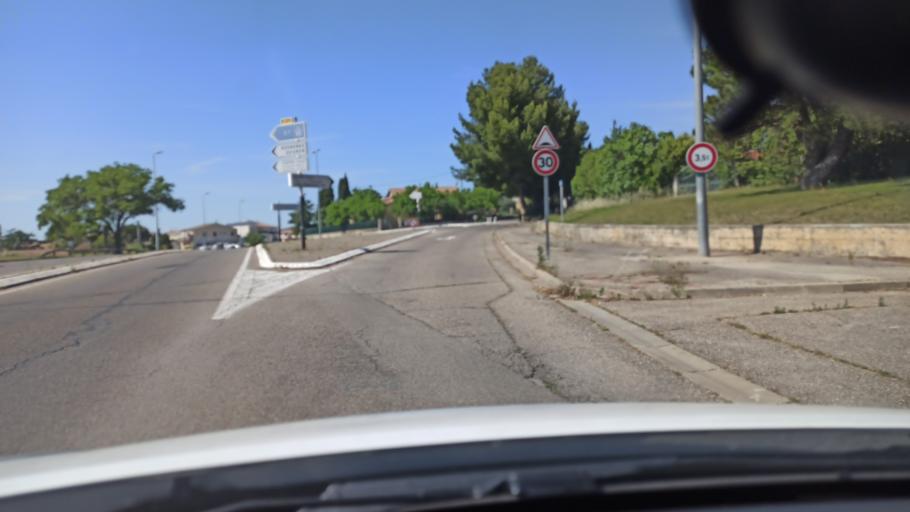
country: FR
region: Provence-Alpes-Cote d'Azur
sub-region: Departement des Bouches-du-Rhone
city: Chateaurenard
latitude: 43.8753
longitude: 4.8496
